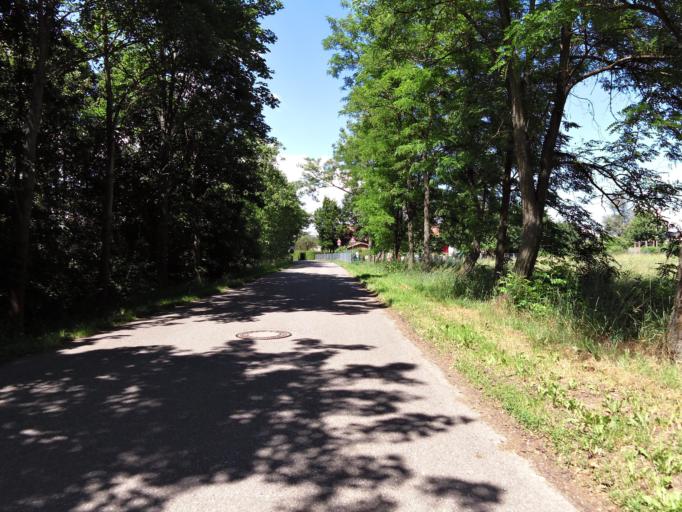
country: DE
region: Rheinland-Pfalz
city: Altdorf
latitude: 49.2831
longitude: 8.2210
